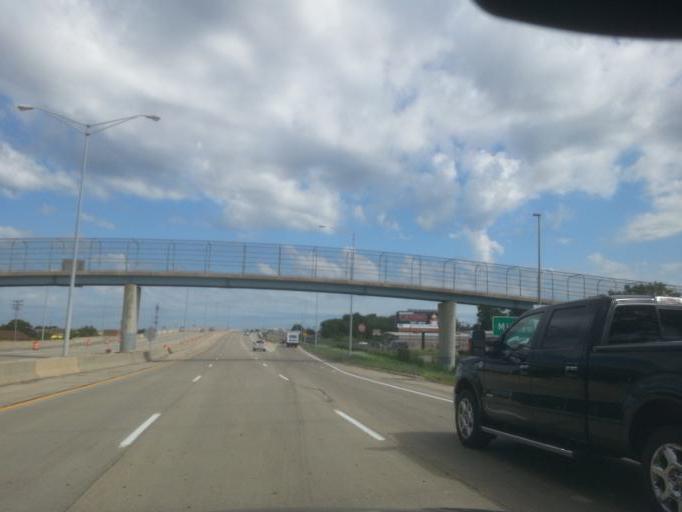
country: US
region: Wisconsin
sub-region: Dane County
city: Monona
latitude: 43.0953
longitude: -89.3153
